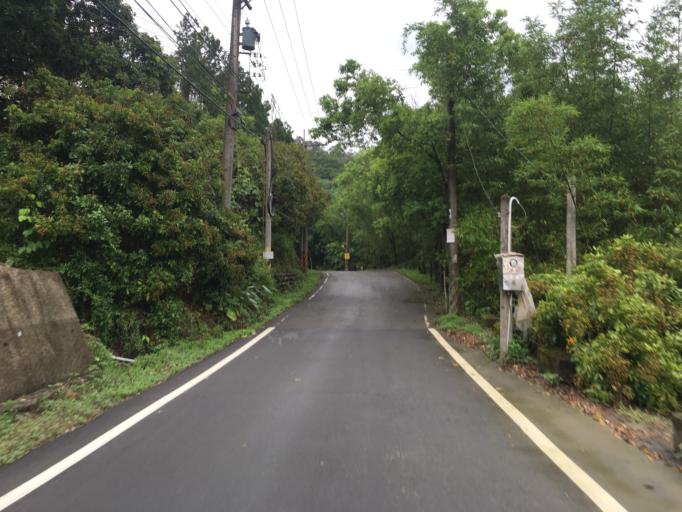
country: TW
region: Taiwan
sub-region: Taichung City
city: Taichung
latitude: 24.0655
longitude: 120.7407
